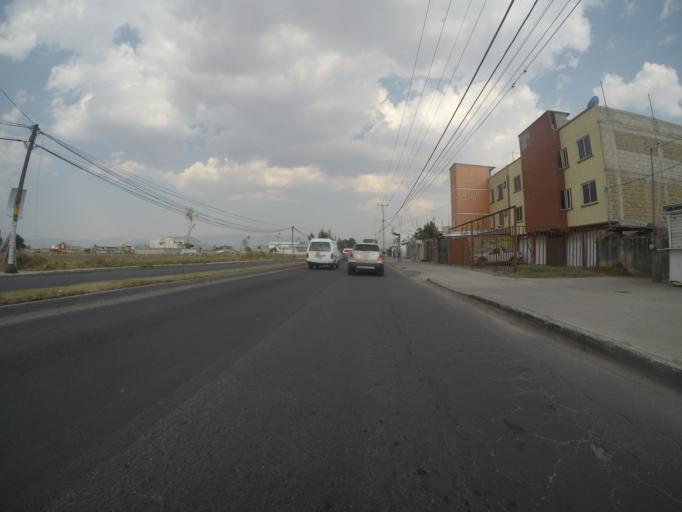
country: MX
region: Mexico
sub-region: Atizapan
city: Colonia la Libertad
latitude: 19.1849
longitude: -99.5069
